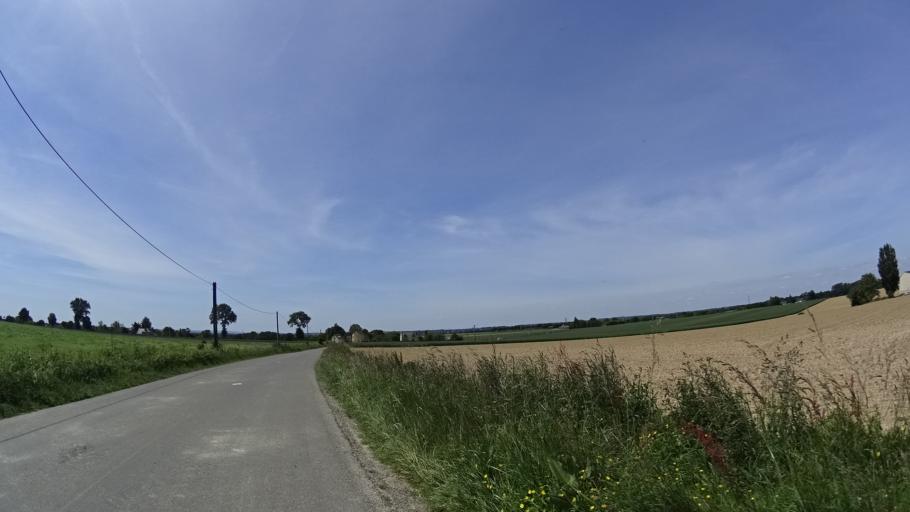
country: FR
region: Brittany
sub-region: Departement d'Ille-et-Vilaine
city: Romille
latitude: 48.1952
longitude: -1.8618
